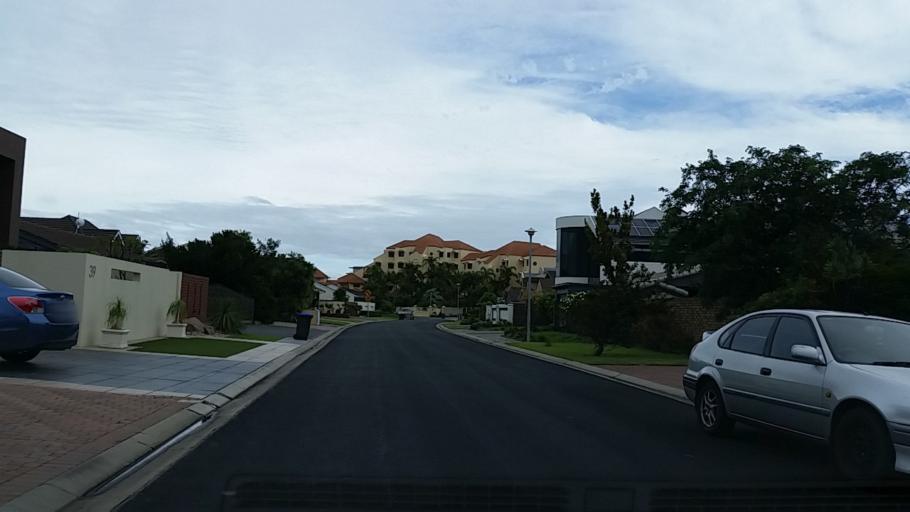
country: AU
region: South Australia
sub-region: Charles Sturt
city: West Lakes Shore
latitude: -34.8747
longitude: 138.4877
